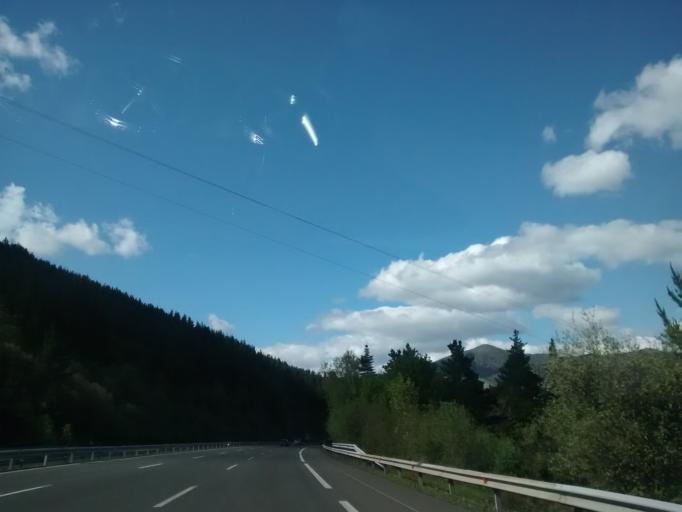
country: ES
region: Basque Country
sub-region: Bizkaia
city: Elexalde
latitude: 43.0929
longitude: -2.9182
